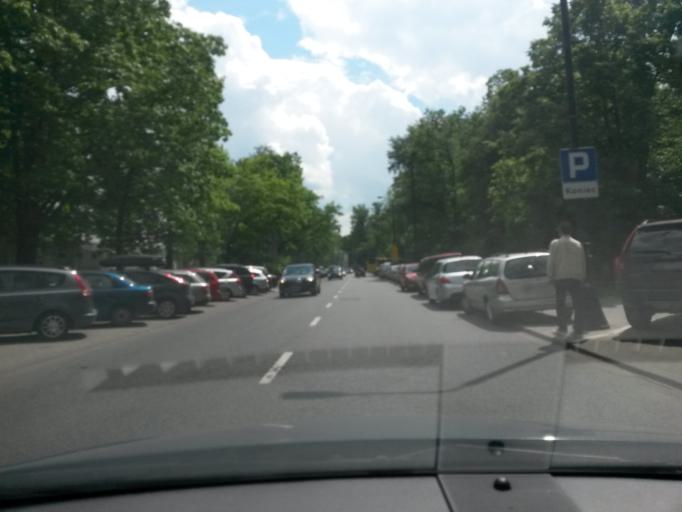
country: PL
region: Masovian Voivodeship
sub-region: Warszawa
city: Srodmiescie
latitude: 52.2191
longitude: 21.0369
